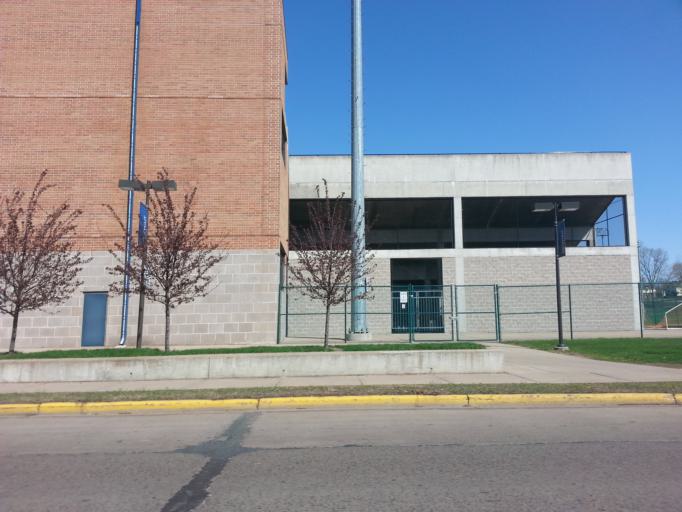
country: US
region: Wisconsin
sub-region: Dunn County
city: Menomonie
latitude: 44.8679
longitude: -91.9297
